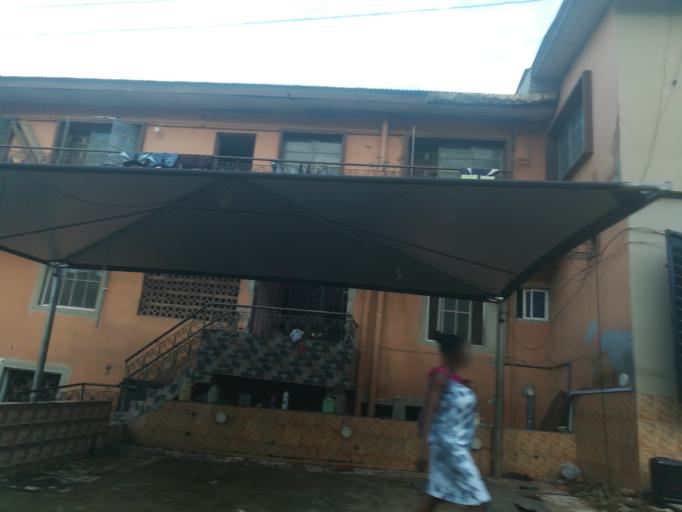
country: NG
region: Lagos
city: Ikorodu
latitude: 6.6254
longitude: 3.4943
